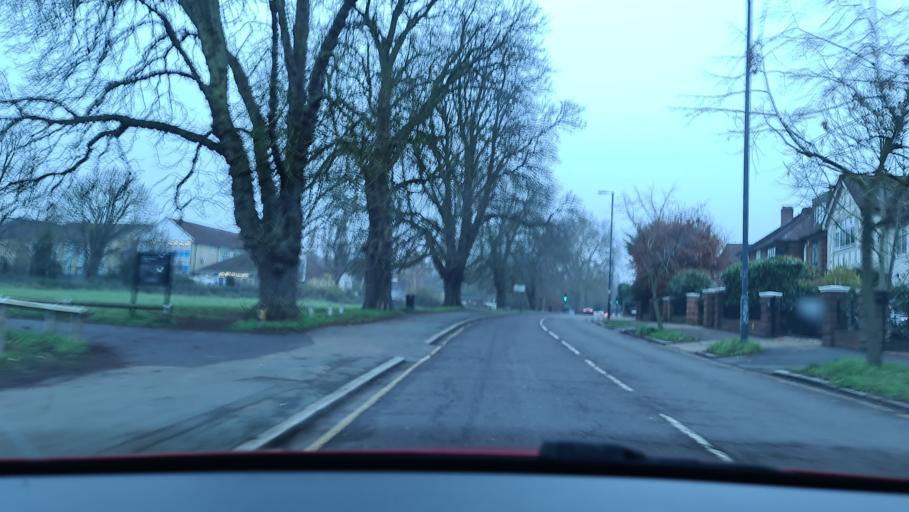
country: GB
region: England
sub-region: Greater London
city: Richmond
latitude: 51.4605
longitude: -0.2890
